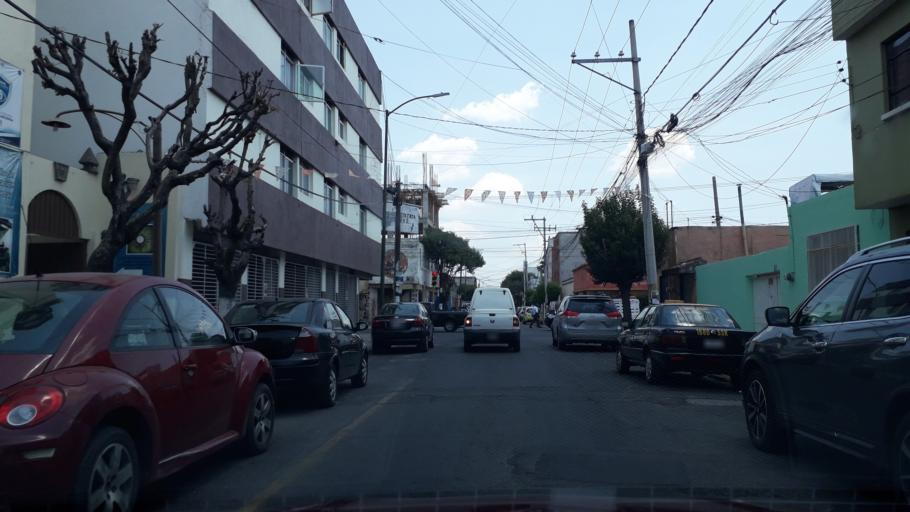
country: MX
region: Puebla
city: Puebla
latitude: 19.0368
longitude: -98.2114
